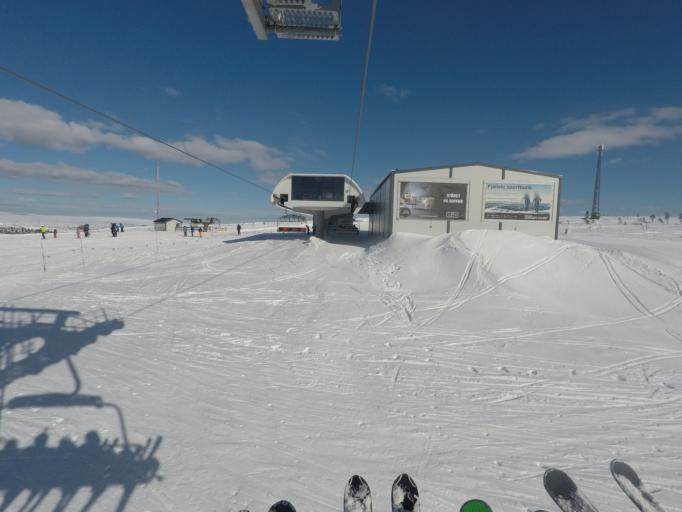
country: NO
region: Hedmark
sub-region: Trysil
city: Innbygda
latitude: 61.1749
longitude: 13.0162
